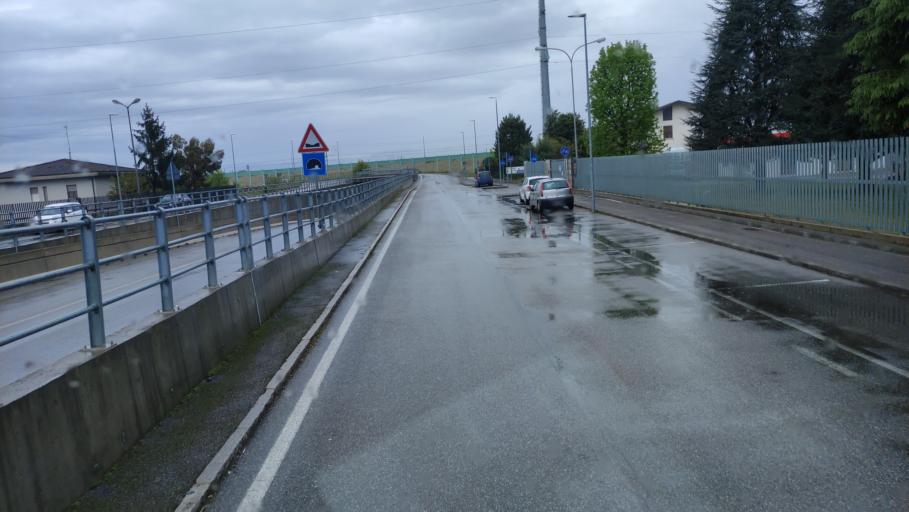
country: IT
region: Lombardy
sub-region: Provincia di Brescia
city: Rudiano
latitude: 45.5011
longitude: 9.8791
